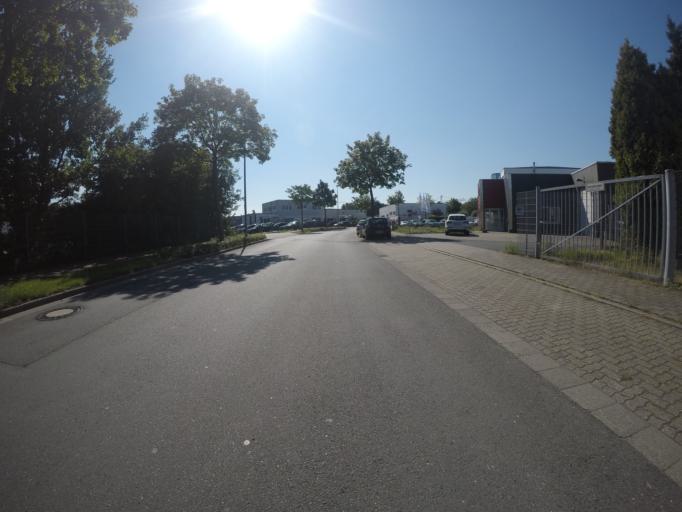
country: DE
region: North Rhine-Westphalia
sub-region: Regierungsbezirk Dusseldorf
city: Bocholt
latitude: 51.8138
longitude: 6.5668
